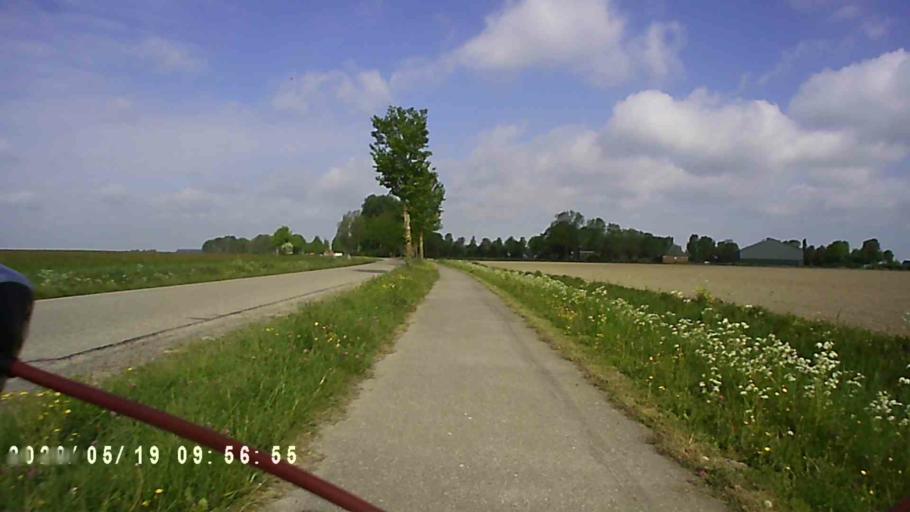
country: NL
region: Groningen
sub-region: Gemeente Zuidhorn
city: Grijpskerk
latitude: 53.2938
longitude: 6.2398
